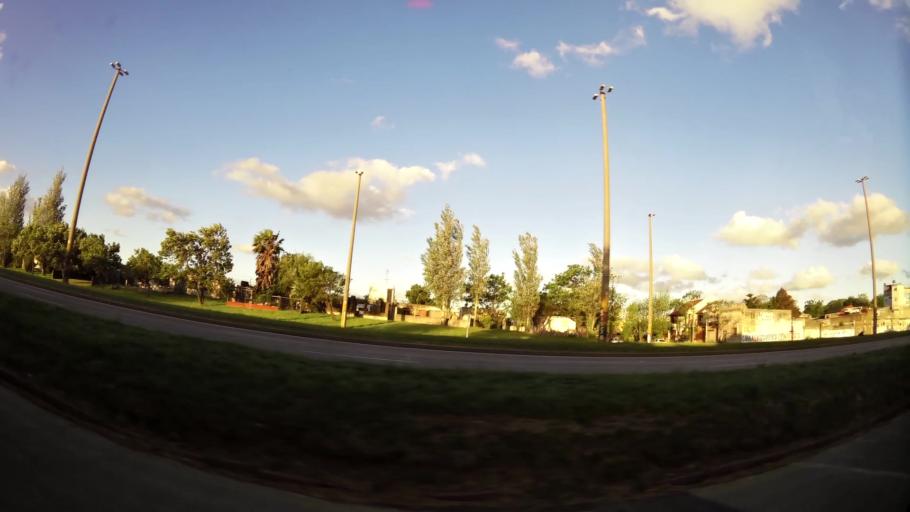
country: UY
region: Montevideo
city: Montevideo
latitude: -34.8708
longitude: -56.2193
